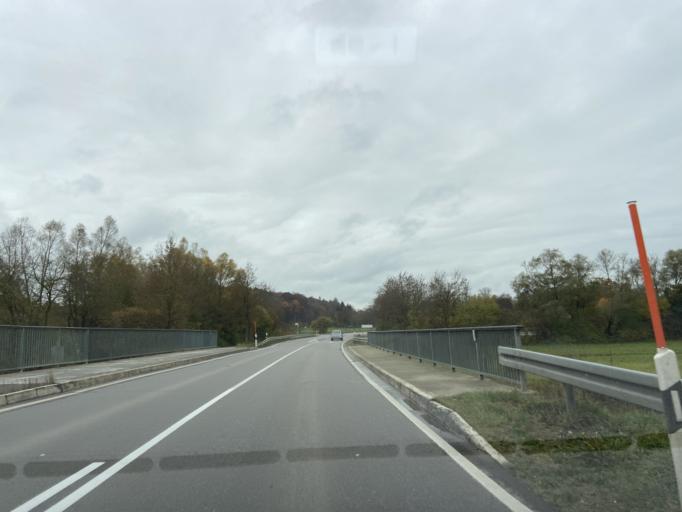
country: DE
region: Baden-Wuerttemberg
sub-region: Tuebingen Region
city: Krauchenwies
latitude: 48.0301
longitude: 9.2490
